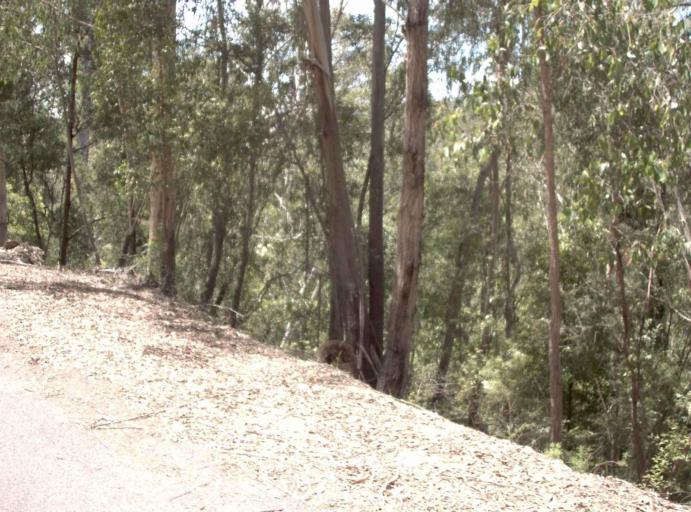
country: AU
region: New South Wales
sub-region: Bombala
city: Bombala
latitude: -37.5019
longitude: 148.9251
